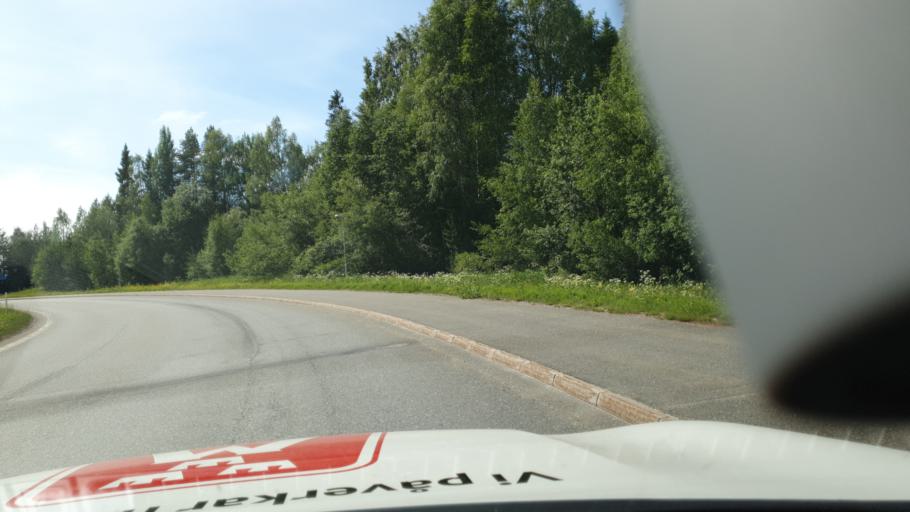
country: SE
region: Vaesterbotten
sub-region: Skelleftea Kommun
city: Byske
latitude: 64.9528
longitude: 21.1906
